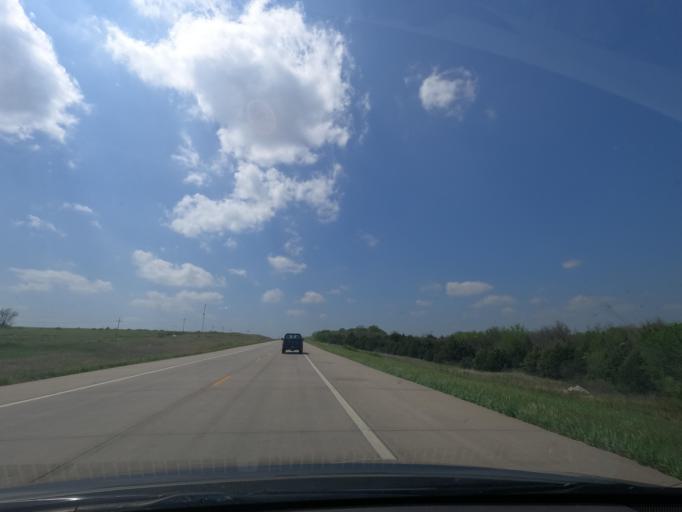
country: US
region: Kansas
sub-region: Elk County
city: Howard
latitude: 37.6330
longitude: -96.1514
